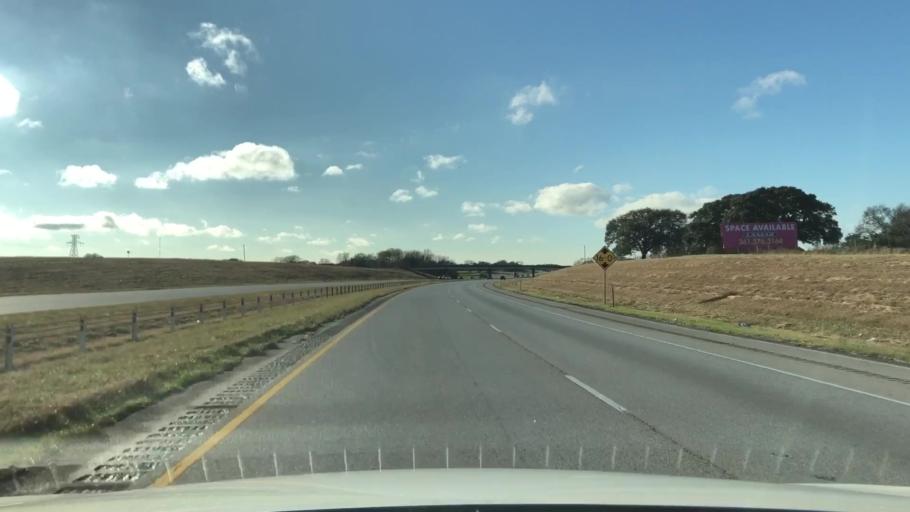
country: US
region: Texas
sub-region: Colorado County
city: Weimar
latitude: 29.6884
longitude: -96.7007
